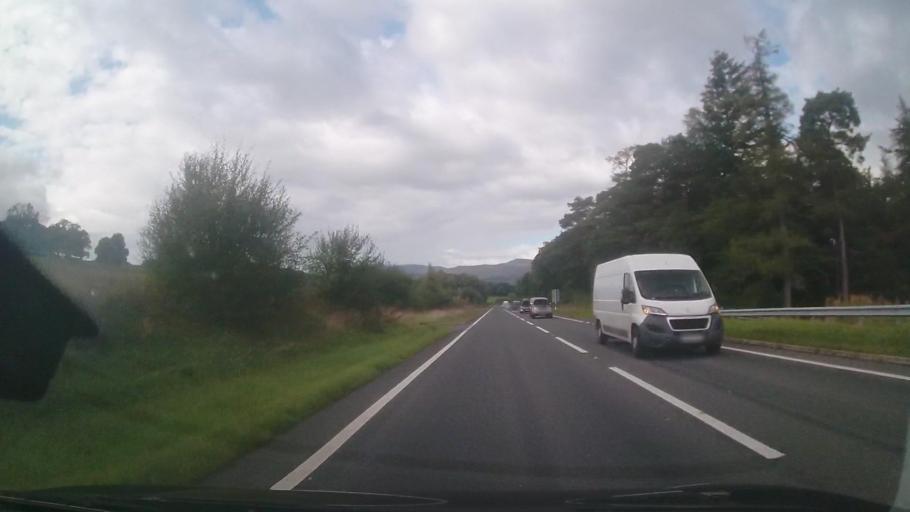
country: GB
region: Wales
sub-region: Gwynedd
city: Dolgellau
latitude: 52.7396
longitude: -3.8328
